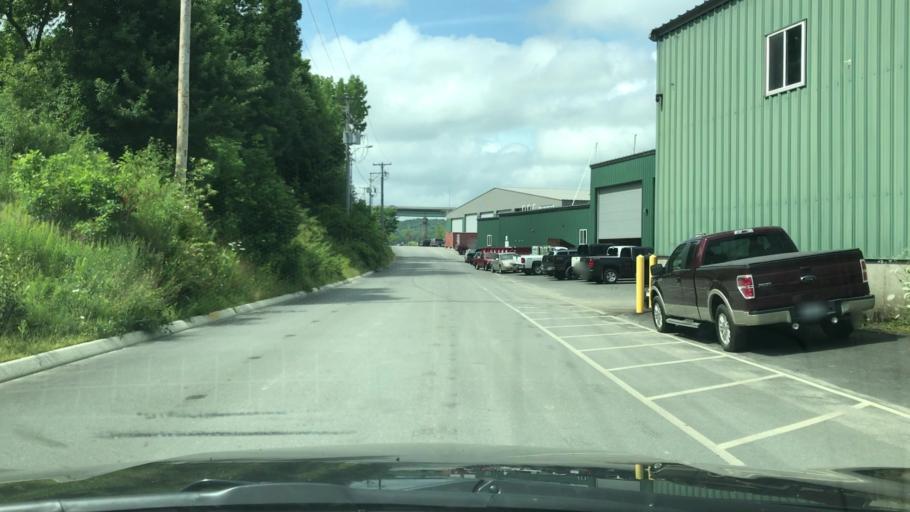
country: US
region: Maine
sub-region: Waldo County
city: Belfast
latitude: 44.4292
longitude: -69.0093
